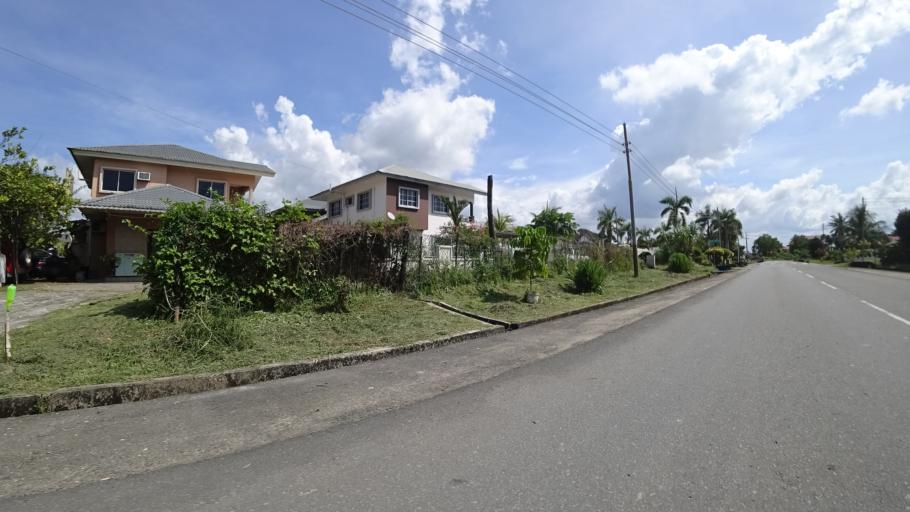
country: BN
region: Brunei and Muara
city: Bandar Seri Begawan
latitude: 4.8854
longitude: 114.8490
